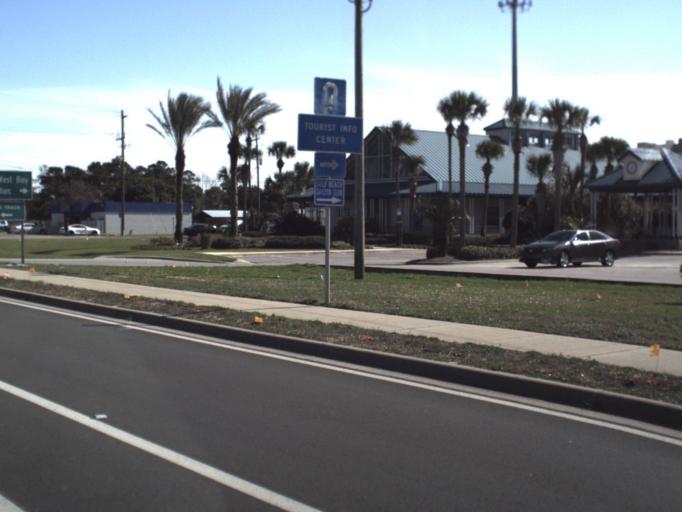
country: US
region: Florida
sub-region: Bay County
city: Laguna Beach
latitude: 30.2303
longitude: -85.8887
